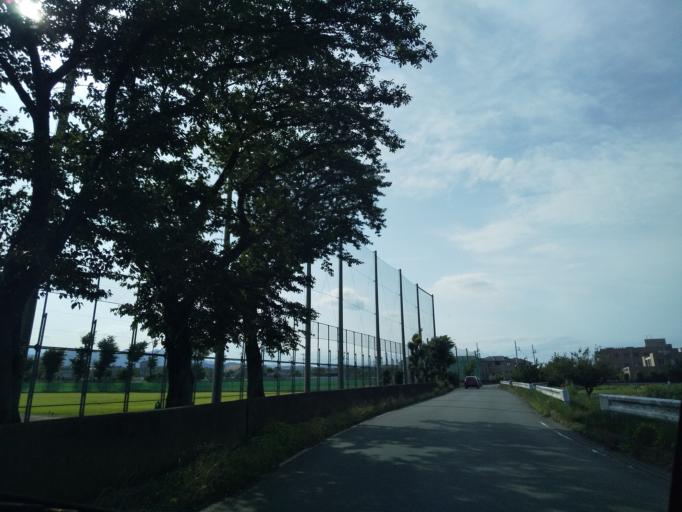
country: JP
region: Kanagawa
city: Zama
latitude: 35.4776
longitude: 139.3811
